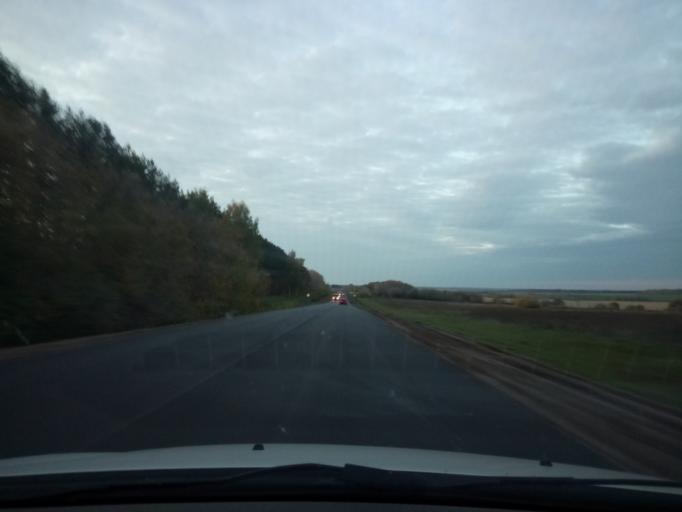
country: RU
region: Nizjnij Novgorod
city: Bol'shoye Murashkino
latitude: 55.8331
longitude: 44.7541
